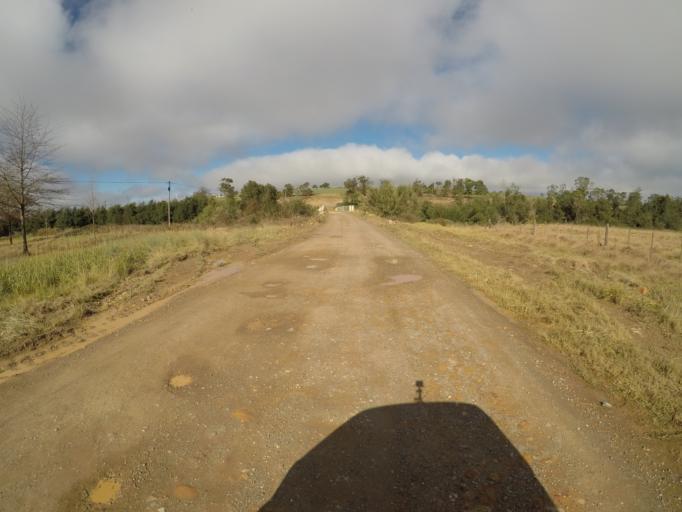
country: ZA
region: Western Cape
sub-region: Cape Winelands District Municipality
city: Ashton
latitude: -34.1275
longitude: 19.8400
